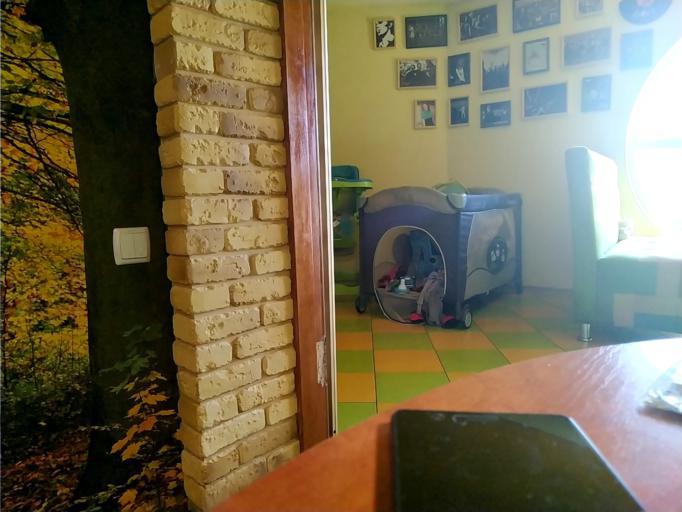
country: RU
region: Rjazan
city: Putyatino
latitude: 54.0786
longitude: 41.1649
